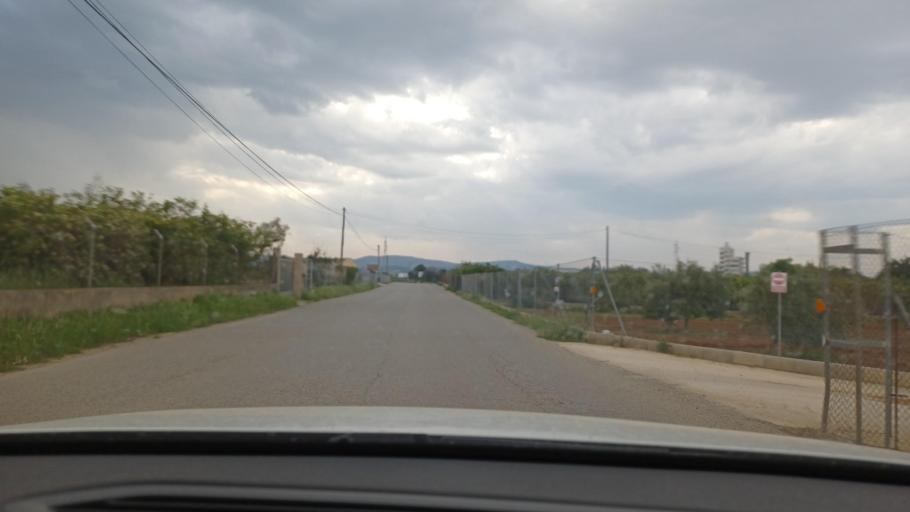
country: ES
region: Valencia
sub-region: Provincia de Castello
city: Benicarlo
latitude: 40.4067
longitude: 0.4002
